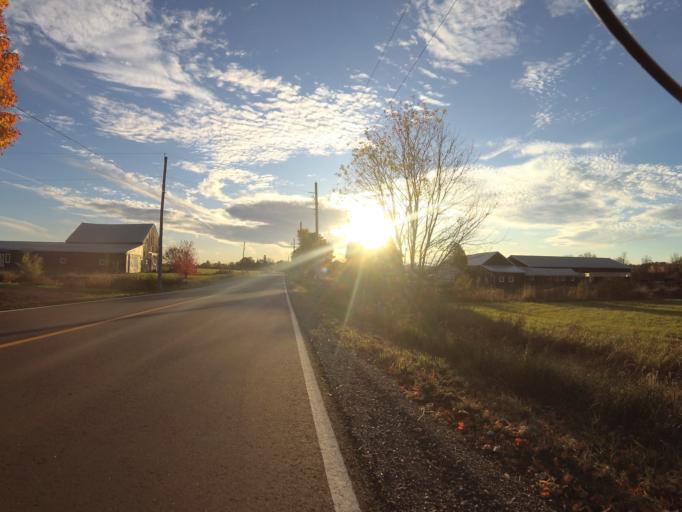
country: CA
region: Ontario
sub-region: Lanark County
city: Smiths Falls
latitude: 44.9652
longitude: -75.8089
